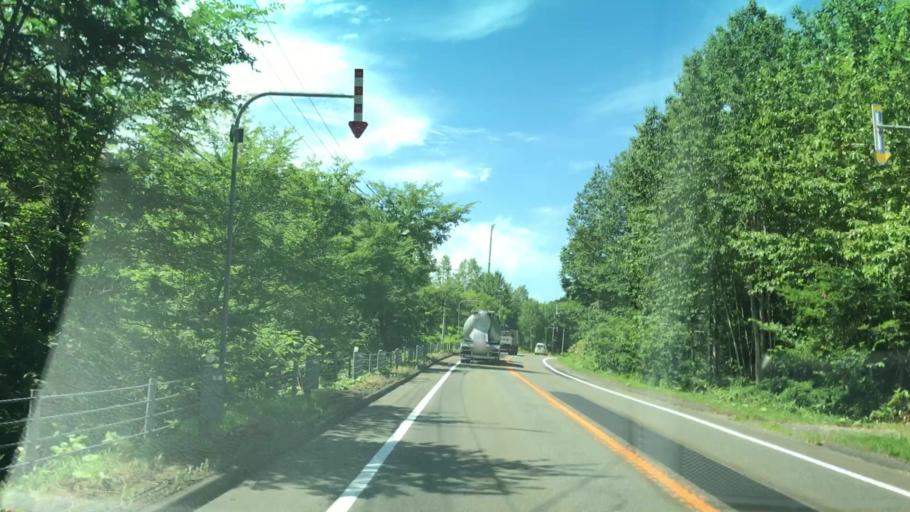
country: JP
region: Hokkaido
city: Shimo-furano
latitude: 42.9103
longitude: 142.4450
